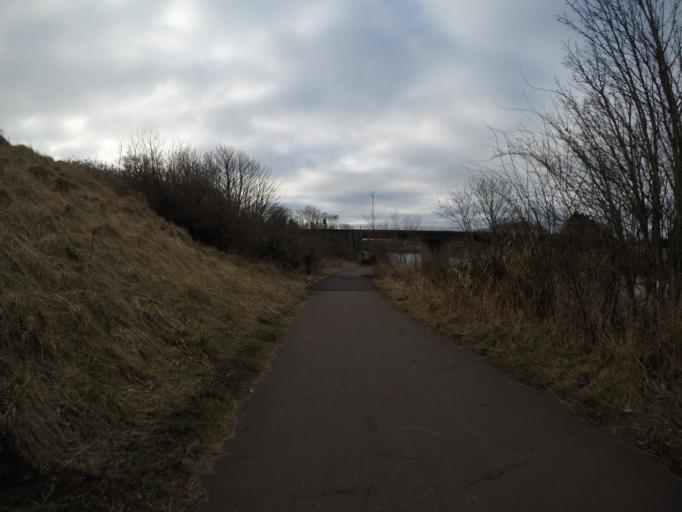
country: GB
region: Scotland
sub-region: North Ayrshire
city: Irvine
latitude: 55.6194
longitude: -4.6729
